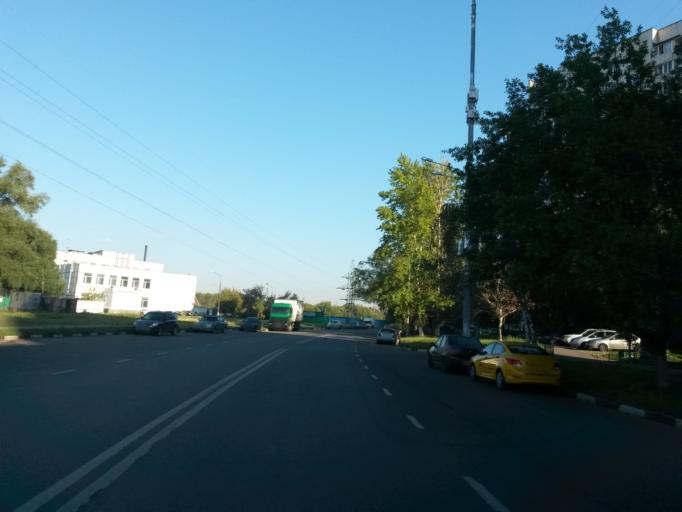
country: RU
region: Moscow
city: Mar'ino
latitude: 55.6487
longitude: 37.7087
